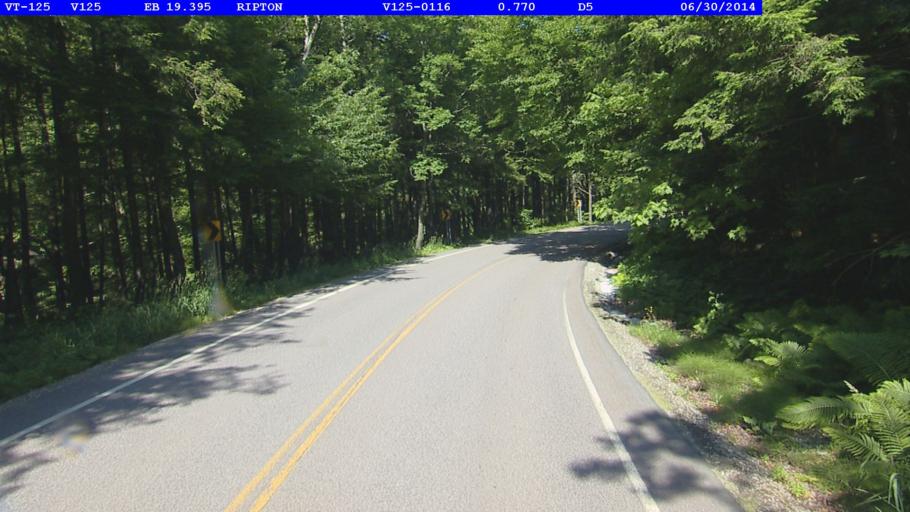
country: US
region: Vermont
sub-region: Addison County
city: Middlebury (village)
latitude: 43.9750
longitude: -73.0458
